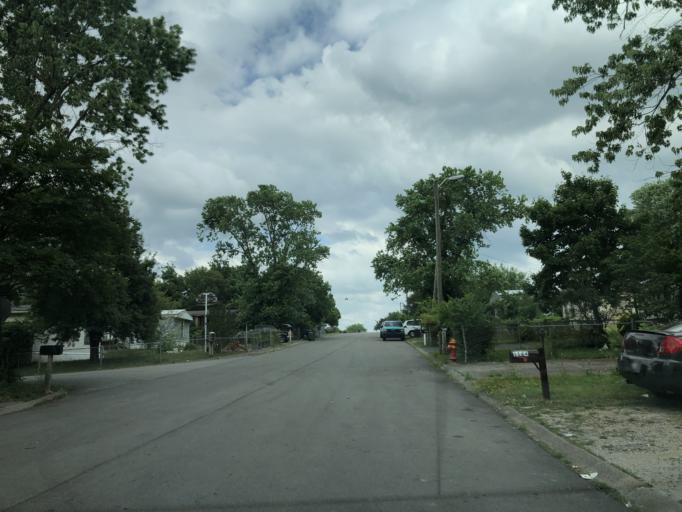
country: US
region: Tennessee
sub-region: Davidson County
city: Lakewood
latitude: 36.2608
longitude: -86.6830
